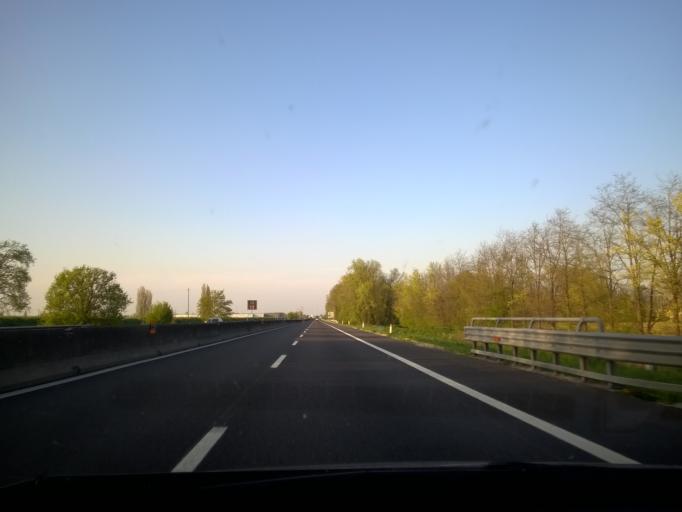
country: IT
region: Emilia-Romagna
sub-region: Provincia di Bologna
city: Bentivoglio
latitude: 44.6112
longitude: 11.4129
